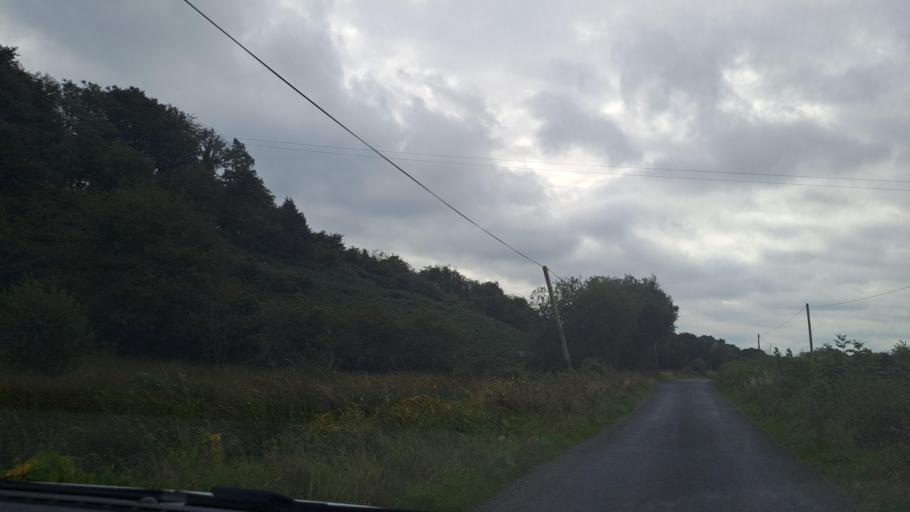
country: IE
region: Ulster
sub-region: An Cabhan
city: Bailieborough
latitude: 53.9438
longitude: -6.9077
